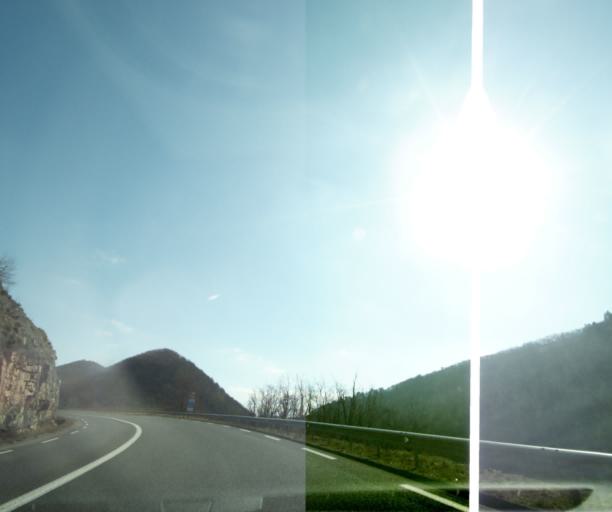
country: FR
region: Midi-Pyrenees
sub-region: Departement de l'Aveyron
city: Saint-Affrique
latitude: 43.9558
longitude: 2.9512
